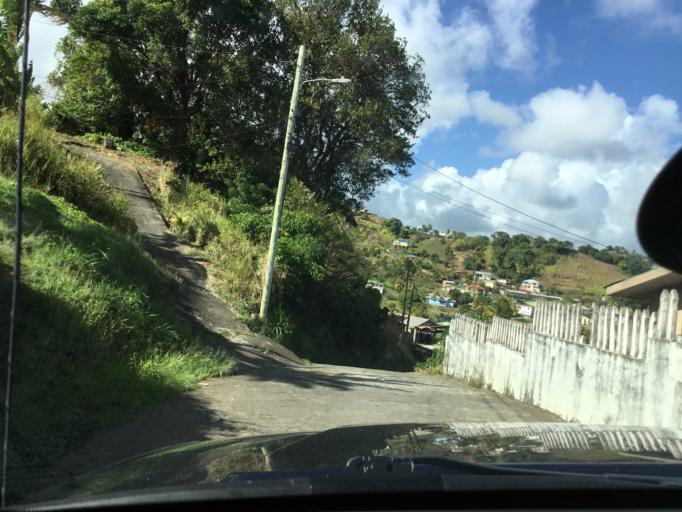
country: VC
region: Charlotte
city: Biabou
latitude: 13.1573
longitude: -61.1679
